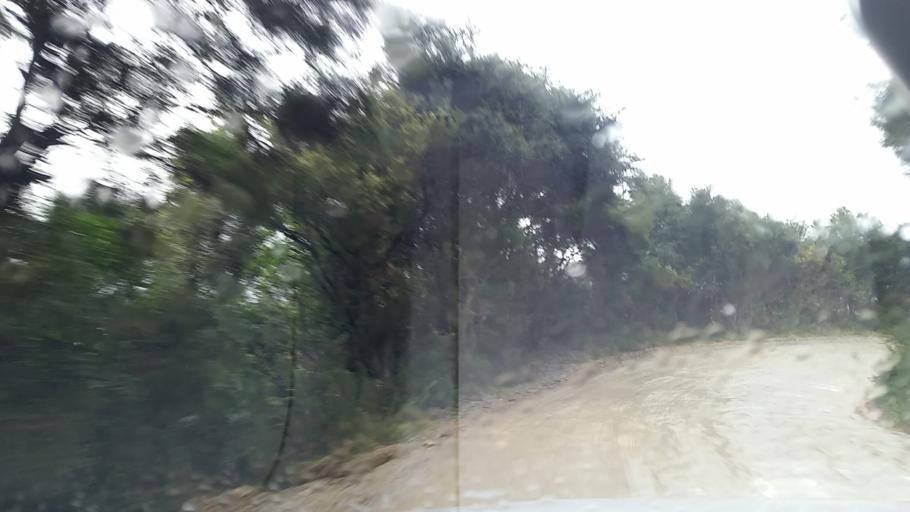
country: NZ
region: Marlborough
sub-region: Marlborough District
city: Picton
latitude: -41.1771
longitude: 174.0798
